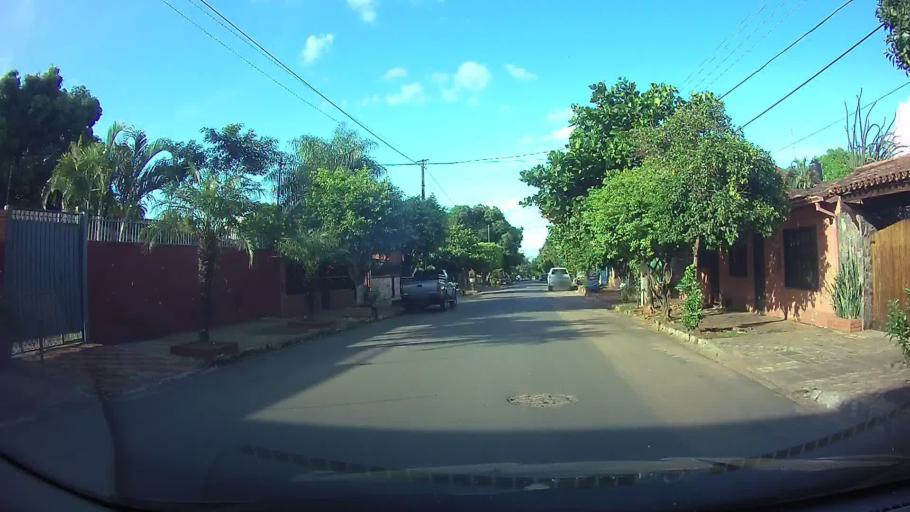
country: PY
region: Central
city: San Lorenzo
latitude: -25.2705
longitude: -57.4842
